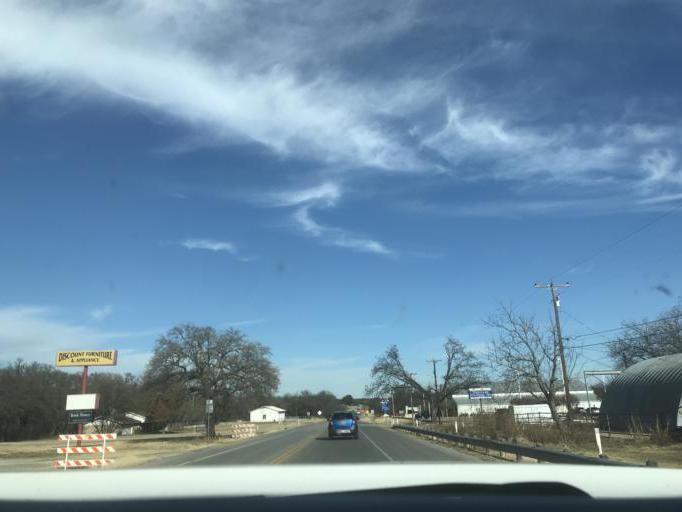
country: US
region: Texas
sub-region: Erath County
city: Stephenville
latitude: 32.2332
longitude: -98.2078
